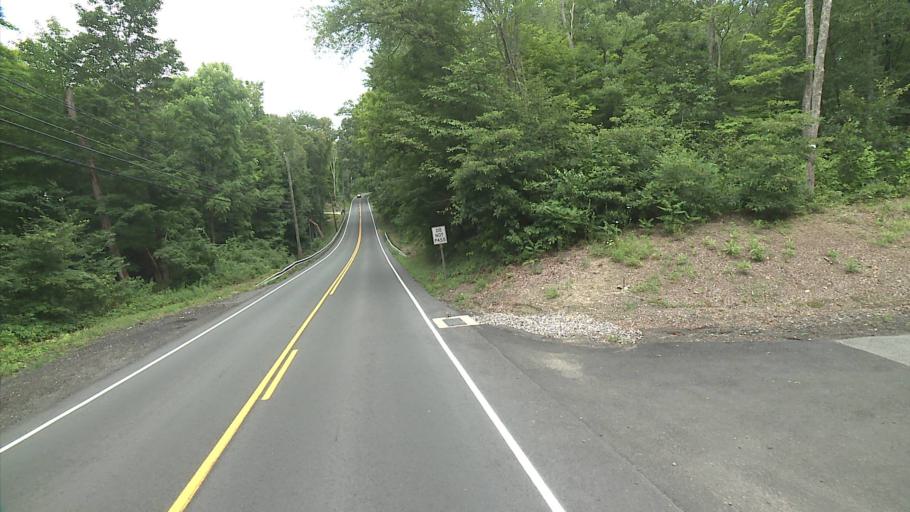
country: US
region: Connecticut
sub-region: Litchfield County
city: Woodbury
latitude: 41.5521
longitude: -73.2988
